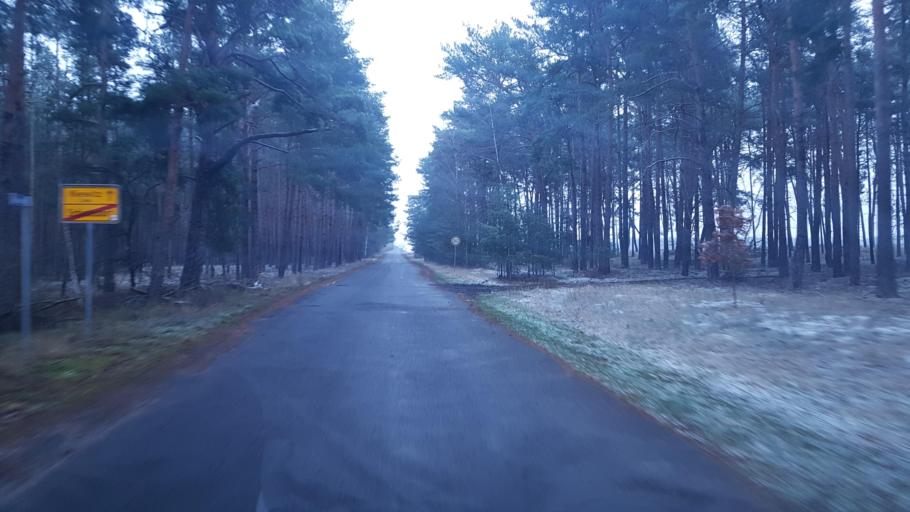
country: DE
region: Brandenburg
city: Kasel-Golzig
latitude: 51.9408
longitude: 13.7531
